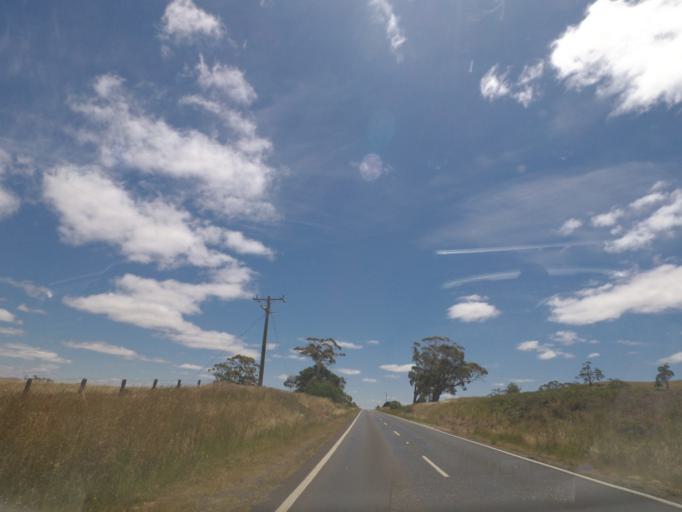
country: AU
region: Victoria
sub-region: Mount Alexander
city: Castlemaine
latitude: -37.2704
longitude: 144.1432
